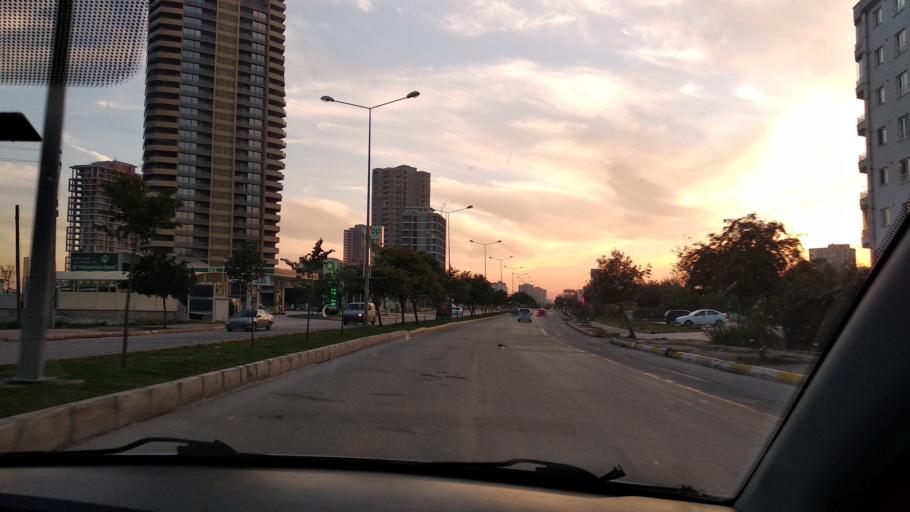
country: TR
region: Mersin
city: Mercin
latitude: 36.8012
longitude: 34.5829
